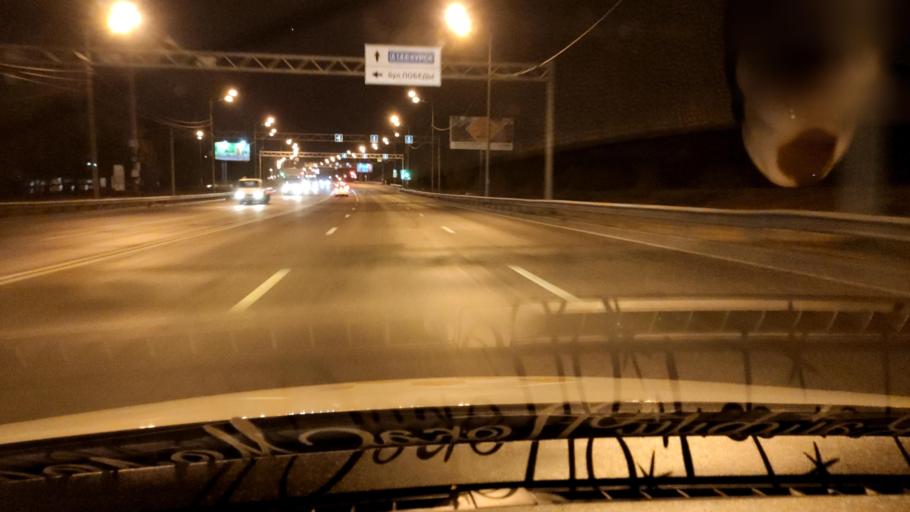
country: RU
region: Voronezj
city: Podgornoye
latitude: 51.7140
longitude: 39.1410
